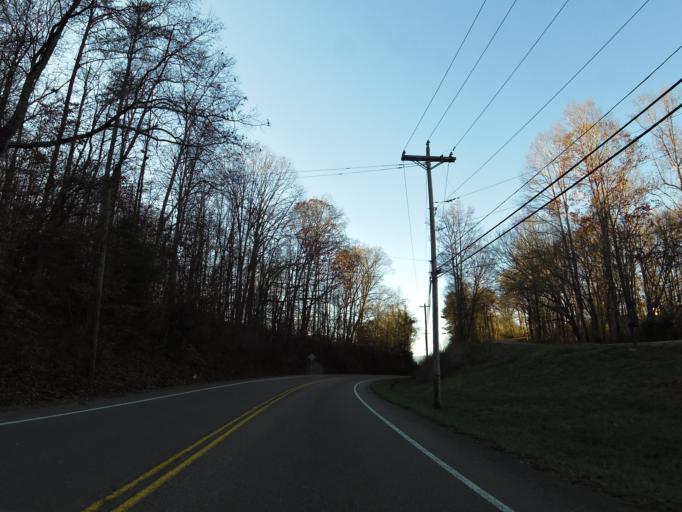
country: US
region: Tennessee
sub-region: Anderson County
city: Oak Ridge
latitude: 36.0667
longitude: -84.2090
